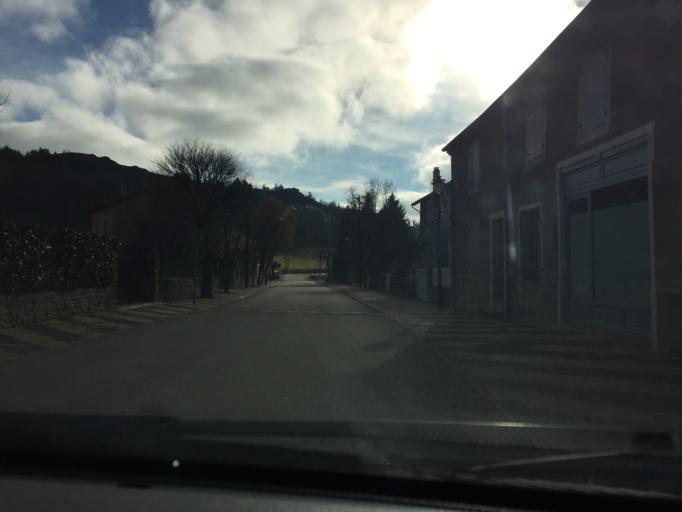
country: FR
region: Languedoc-Roussillon
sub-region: Departement de la Lozere
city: Langogne
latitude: 44.5210
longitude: 3.9089
